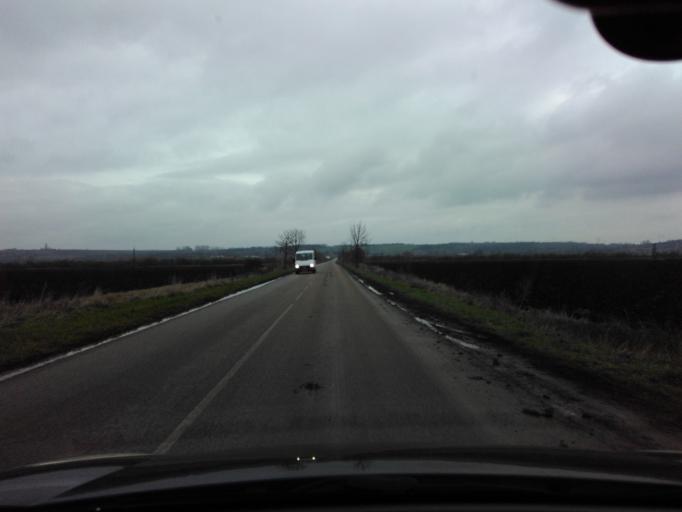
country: HU
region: Heves
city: Hatvan
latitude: 47.6951
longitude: 19.6735
